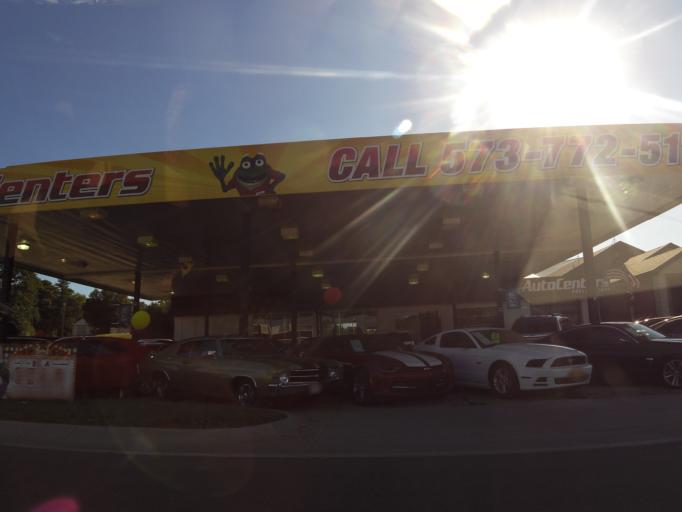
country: US
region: Missouri
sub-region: Butler County
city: Poplar Bluff
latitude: 36.7892
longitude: -90.4322
